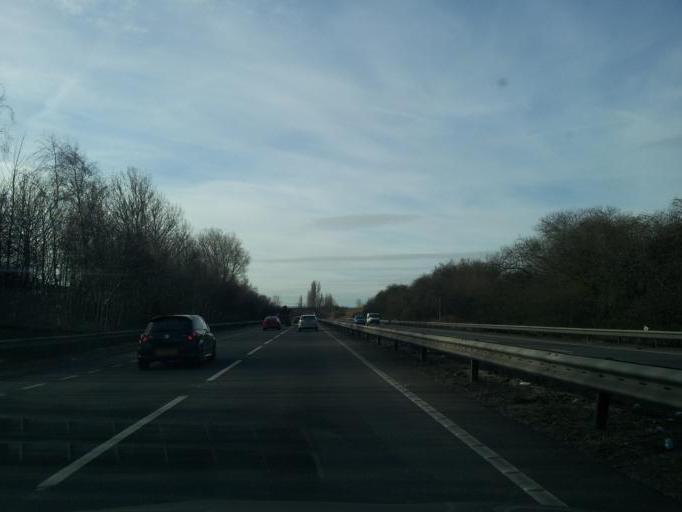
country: GB
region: England
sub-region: Cambridgeshire
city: Eaton Socon
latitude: 52.2236
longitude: -0.2968
